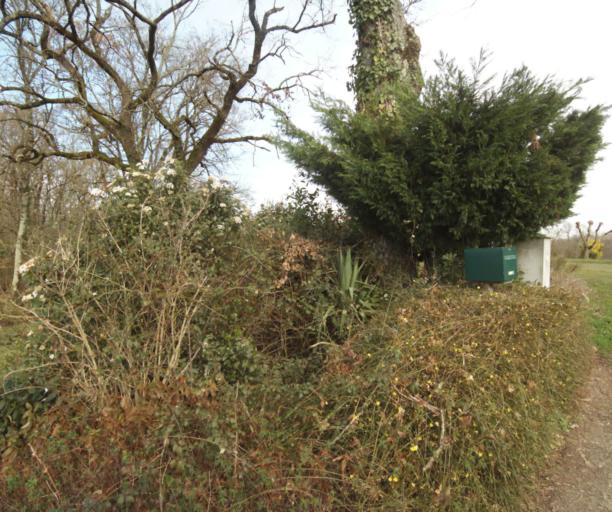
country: FR
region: Aquitaine
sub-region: Departement des Landes
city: Gabarret
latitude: 43.9269
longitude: 0.0562
